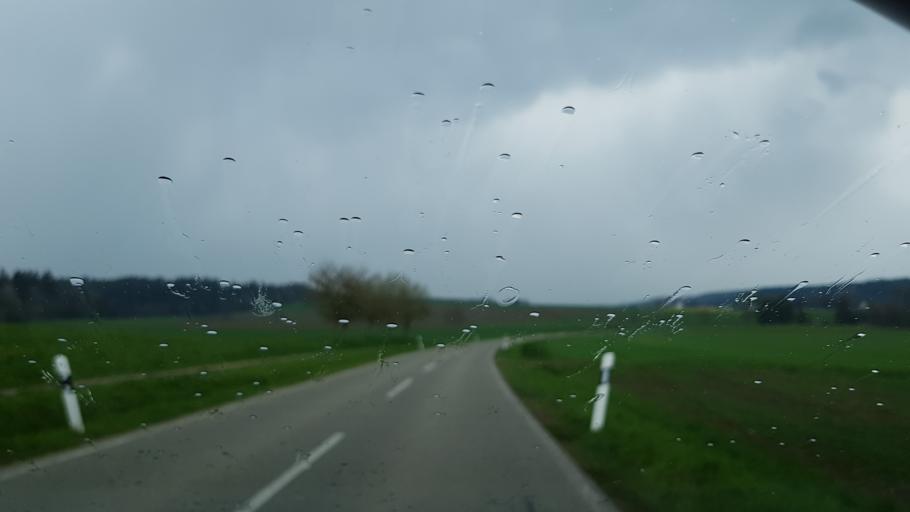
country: DE
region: Baden-Wuerttemberg
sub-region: Tuebingen Region
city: Wain
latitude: 48.2181
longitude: 10.0151
